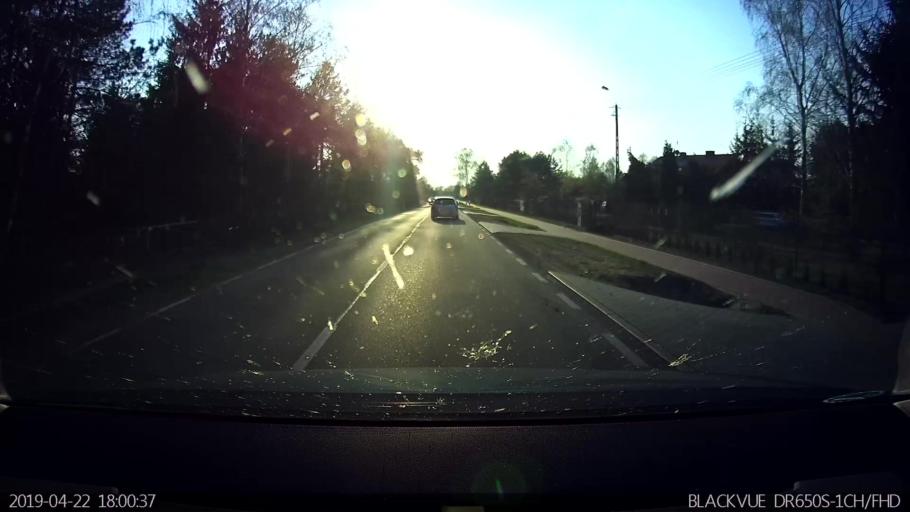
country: PL
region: Masovian Voivodeship
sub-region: Powiat wegrowski
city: Korytnica
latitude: 52.4764
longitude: 21.8436
